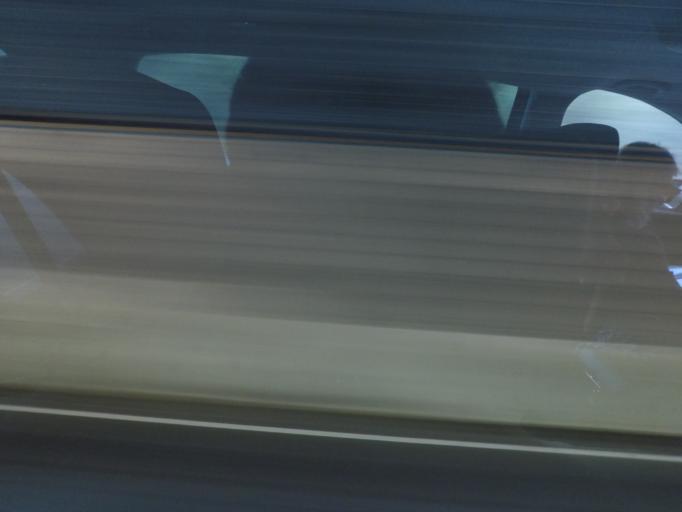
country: IT
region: Aosta Valley
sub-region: Valle d'Aosta
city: Antey-Saint-Andre
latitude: 45.7867
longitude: 7.5914
